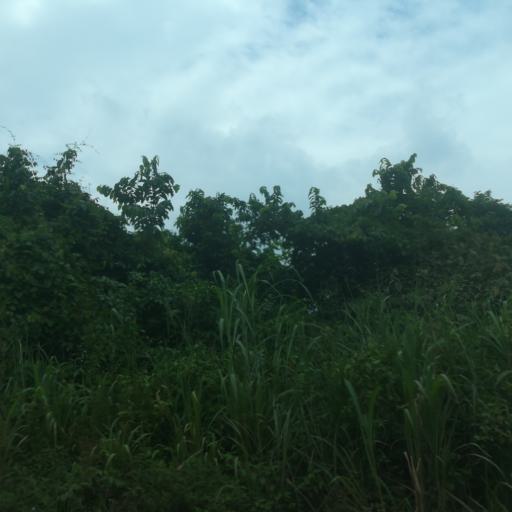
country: NG
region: Lagos
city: Ejirin
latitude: 6.6706
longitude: 3.7974
